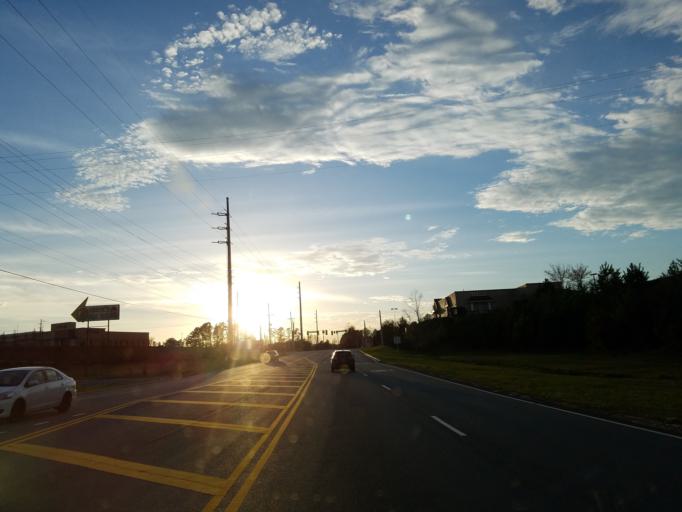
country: US
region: Georgia
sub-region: Dawson County
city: Dawsonville
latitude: 34.3536
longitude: -84.0484
